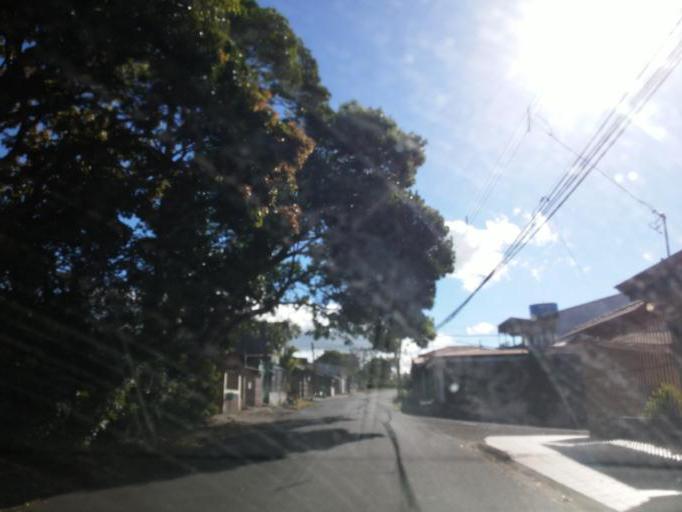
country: CR
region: Alajuela
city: Alajuela
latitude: 10.0282
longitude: -84.2042
